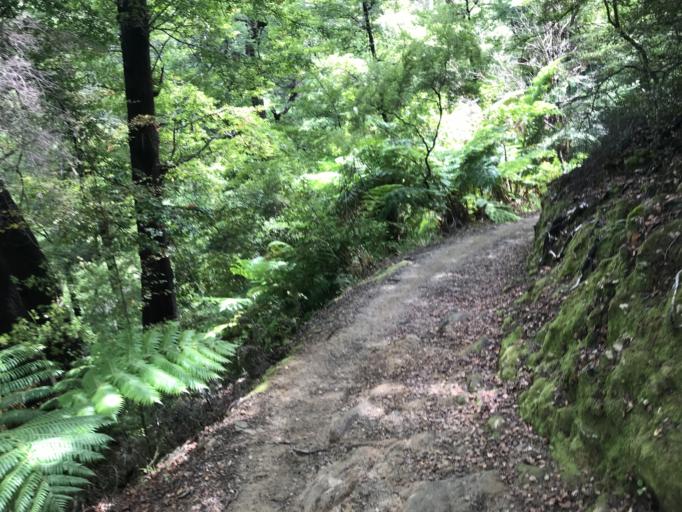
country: NZ
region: Marlborough
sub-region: Marlborough District
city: Picton
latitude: -41.2526
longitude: 173.9520
